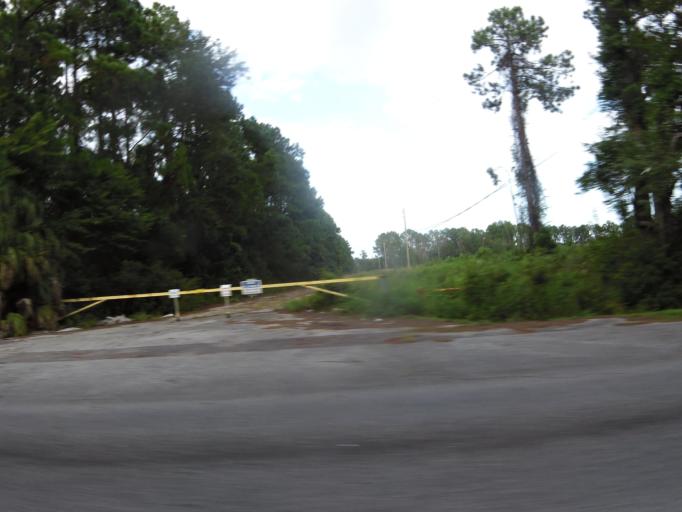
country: US
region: Florida
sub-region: Duval County
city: Jacksonville
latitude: 30.3547
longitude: -81.7521
